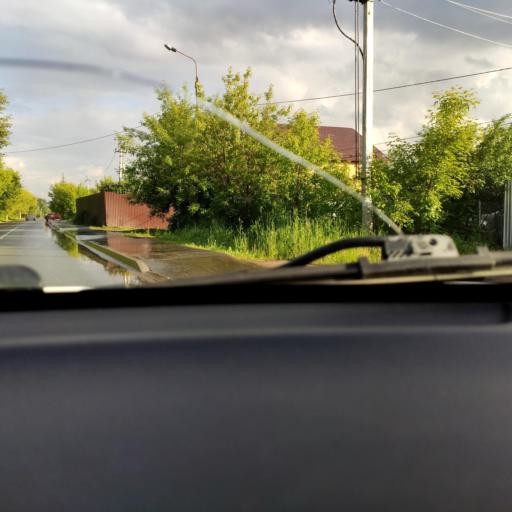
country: RU
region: Tatarstan
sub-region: Gorod Kazan'
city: Kazan
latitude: 55.8378
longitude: 49.1888
